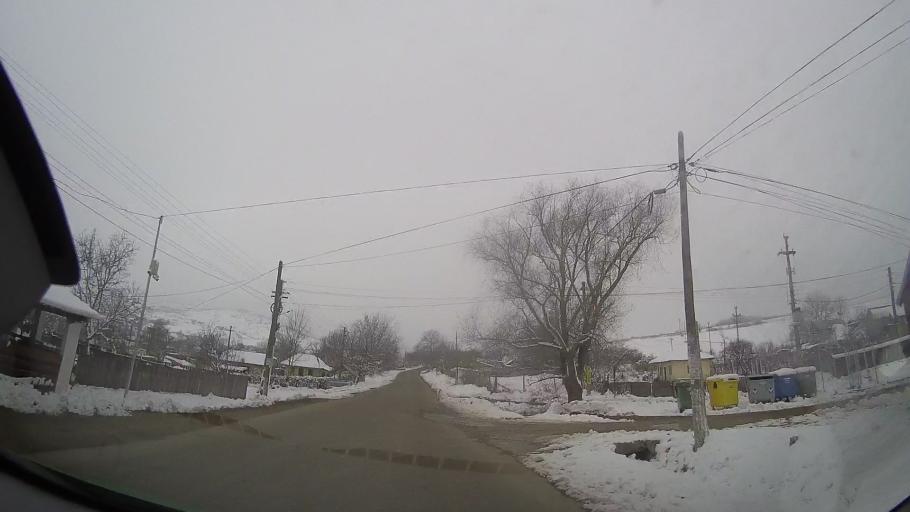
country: RO
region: Neamt
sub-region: Comuna Oniceni
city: Oniceni
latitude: 46.8080
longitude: 27.1841
